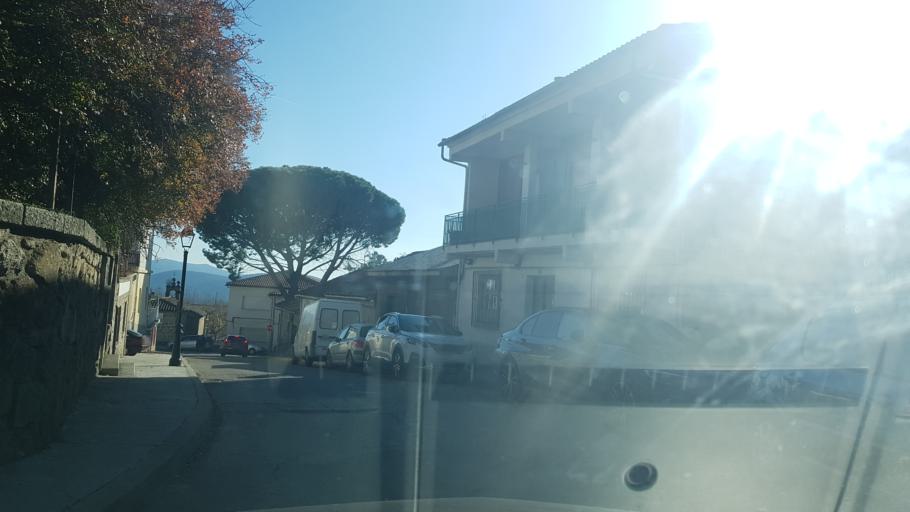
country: ES
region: Castille and Leon
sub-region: Provincia de Avila
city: Piedralaves
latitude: 40.3184
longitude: -4.6967
